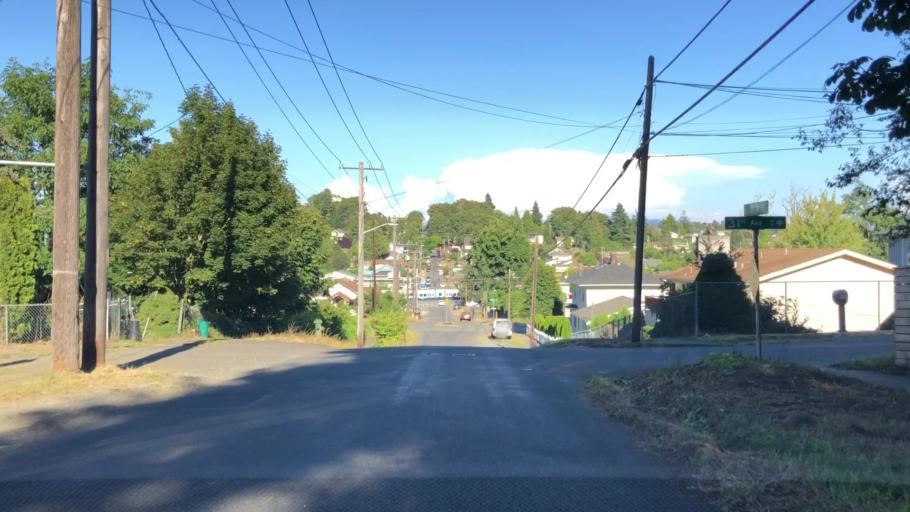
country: US
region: Washington
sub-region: King County
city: Seattle
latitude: 47.5535
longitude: -122.2931
